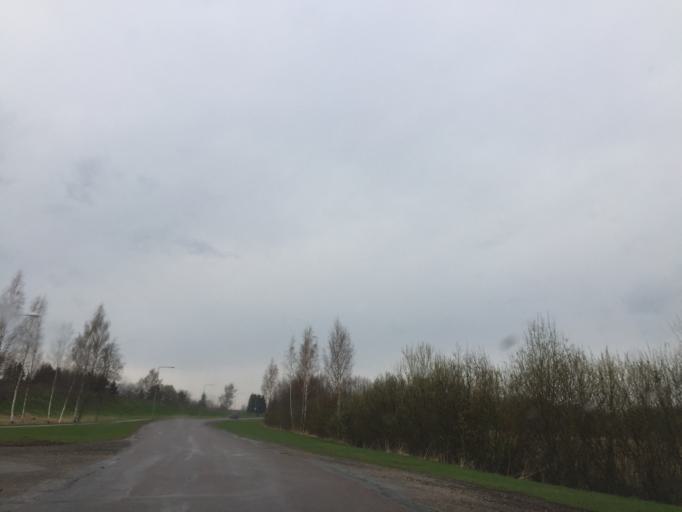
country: EE
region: Tartu
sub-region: UElenurme vald
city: Ulenurme
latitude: 58.3059
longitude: 26.7235
